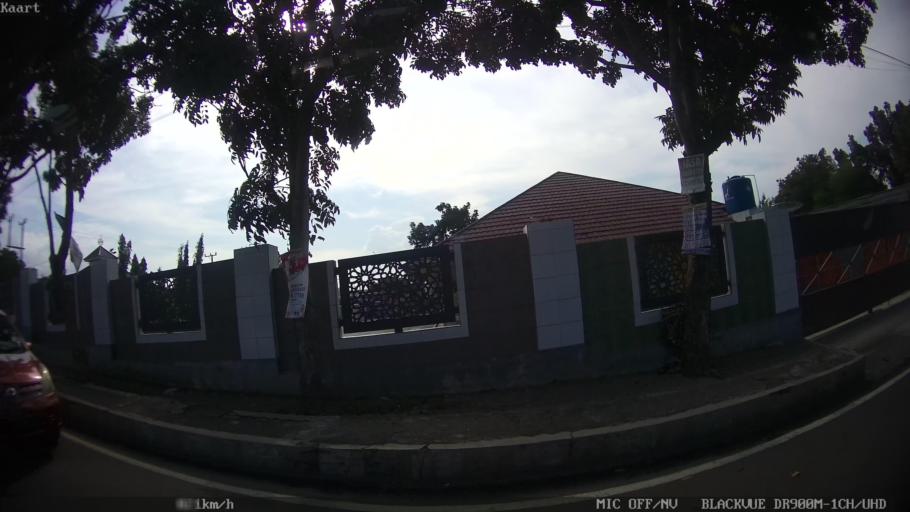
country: ID
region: Lampung
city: Kedaton
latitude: -5.3854
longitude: 105.2214
